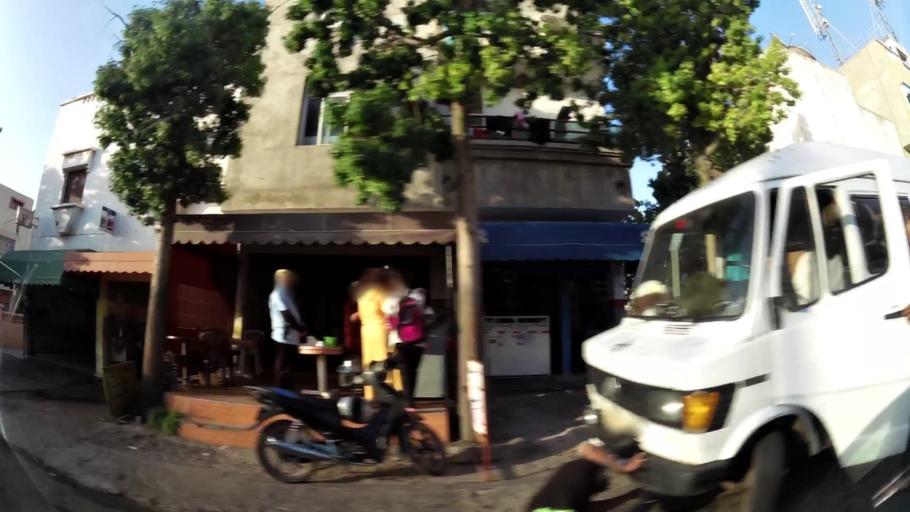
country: MA
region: Oued ed Dahab-Lagouira
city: Dakhla
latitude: 30.4177
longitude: -9.5712
